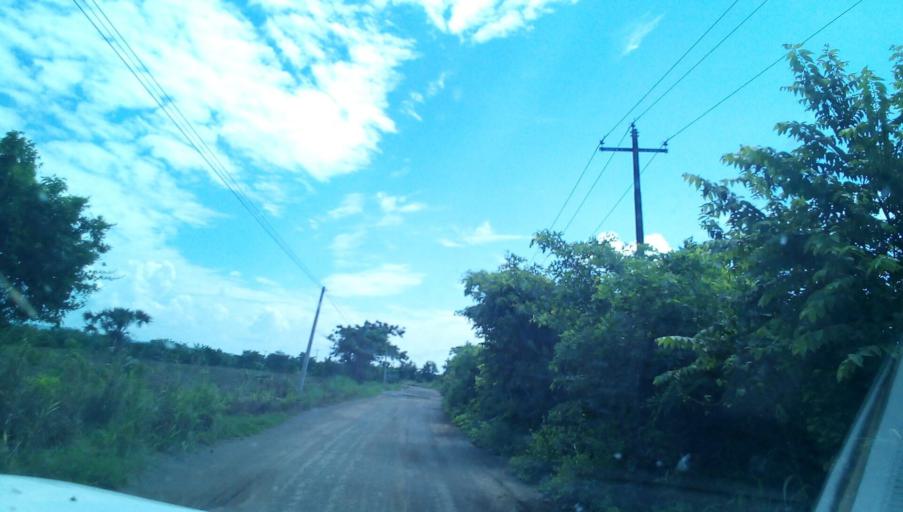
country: MX
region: Veracruz
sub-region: Alamo Temapache
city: Vegas de la Soledad y Soledad Dos
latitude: 20.9032
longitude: -97.9389
